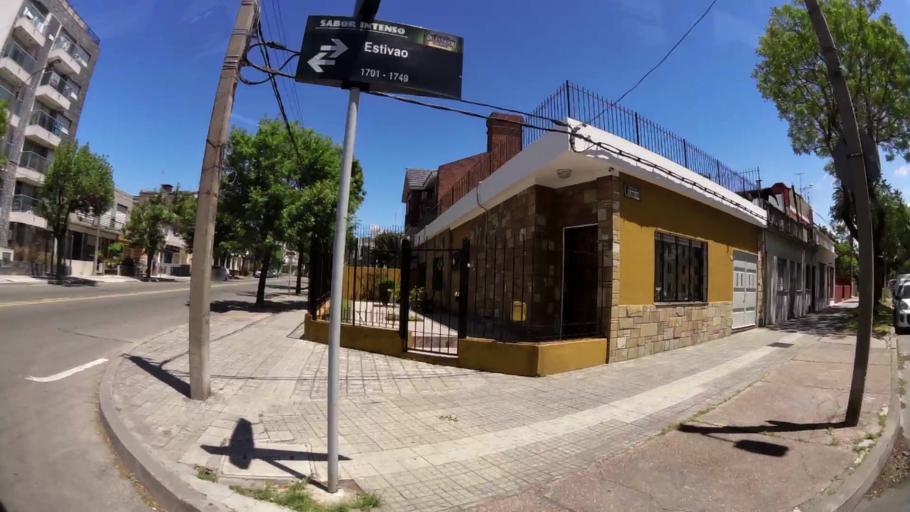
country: UY
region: Montevideo
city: Montevideo
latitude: -34.8936
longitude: -56.1340
